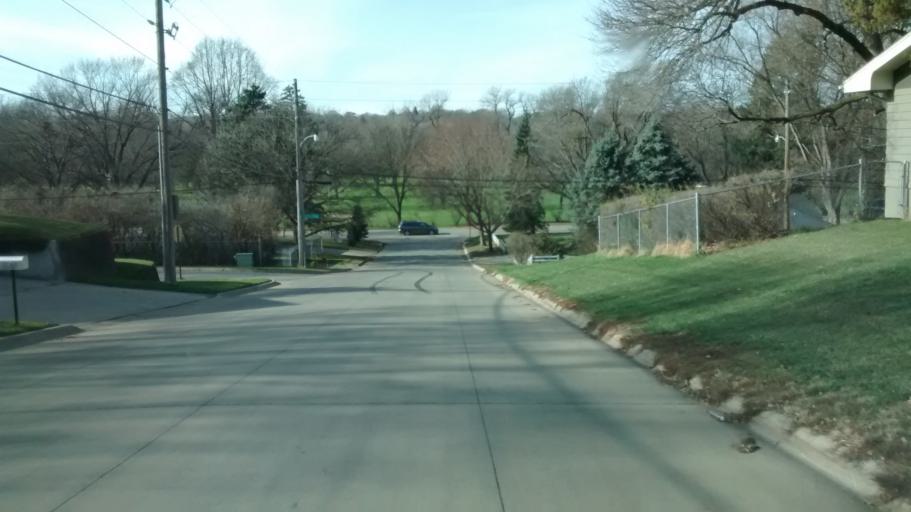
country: US
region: Iowa
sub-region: Woodbury County
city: Sioux City
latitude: 42.5376
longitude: -96.4069
